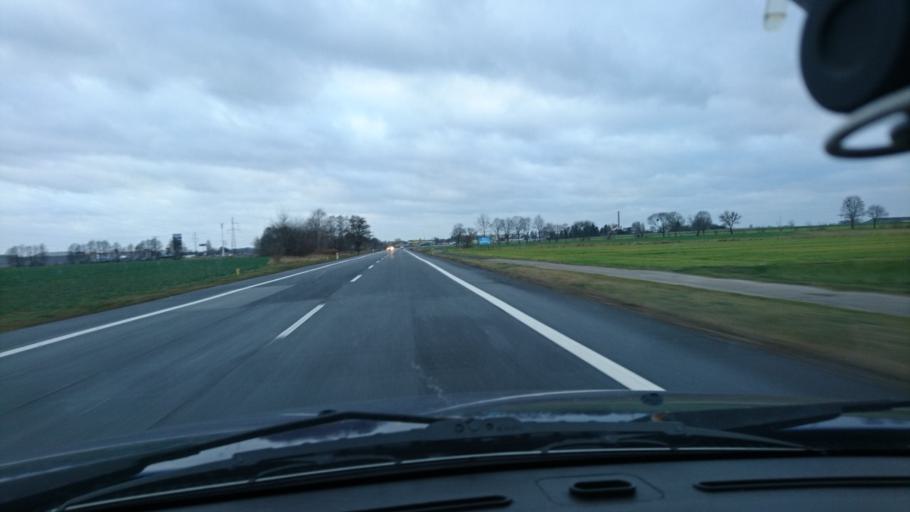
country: PL
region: Opole Voivodeship
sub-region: Powiat kluczborski
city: Kluczbork
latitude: 50.9907
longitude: 18.2212
